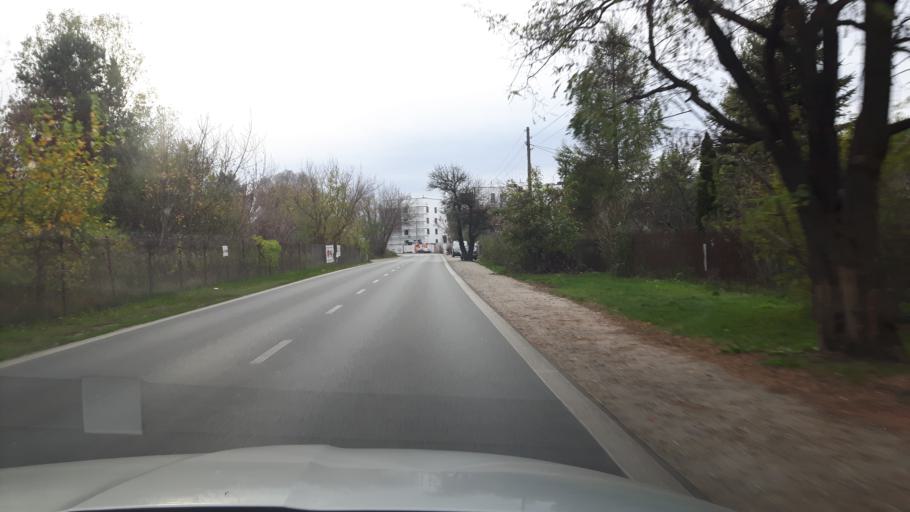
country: PL
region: Masovian Voivodeship
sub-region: Powiat wolominski
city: Zabki
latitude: 52.2777
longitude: 21.0912
